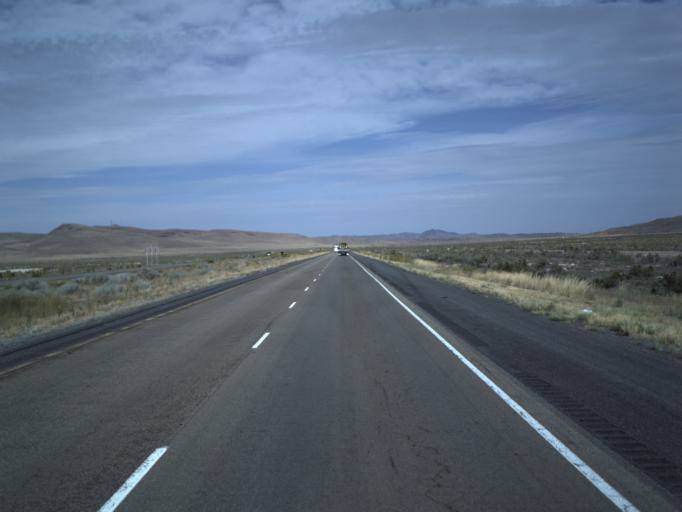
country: US
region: Utah
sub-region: Tooele County
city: Grantsville
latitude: 40.7728
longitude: -112.7993
